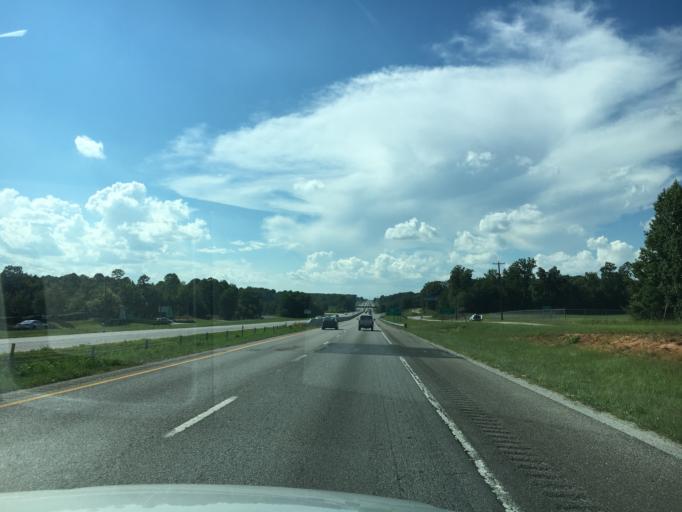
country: US
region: South Carolina
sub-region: Greenville County
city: Fountain Inn
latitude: 34.6758
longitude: -82.1952
